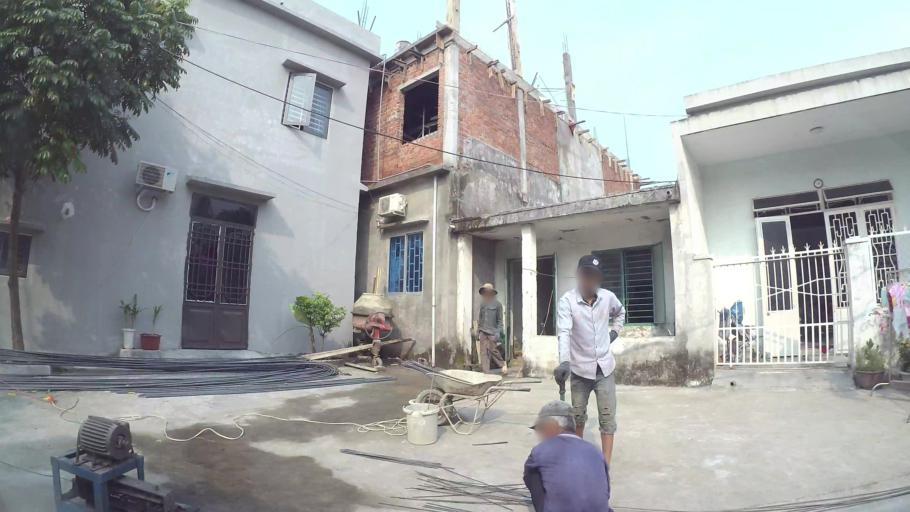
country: VN
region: Da Nang
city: Son Tra
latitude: 16.0938
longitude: 108.2501
